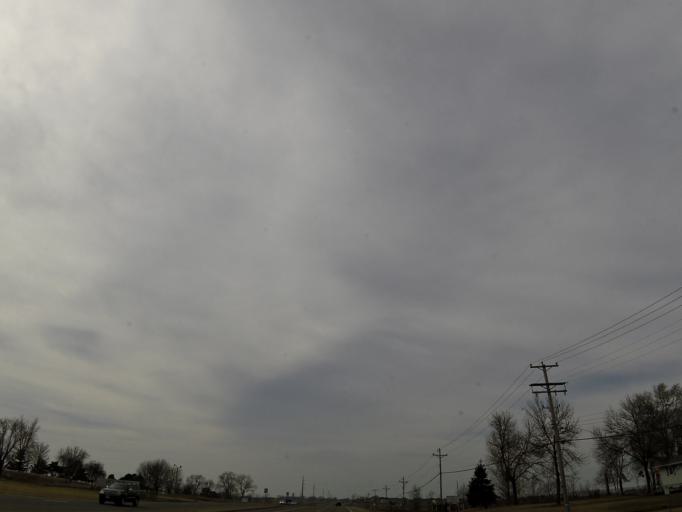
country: US
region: Minnesota
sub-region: Dakota County
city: Rosemount
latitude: 44.7392
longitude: -93.0790
